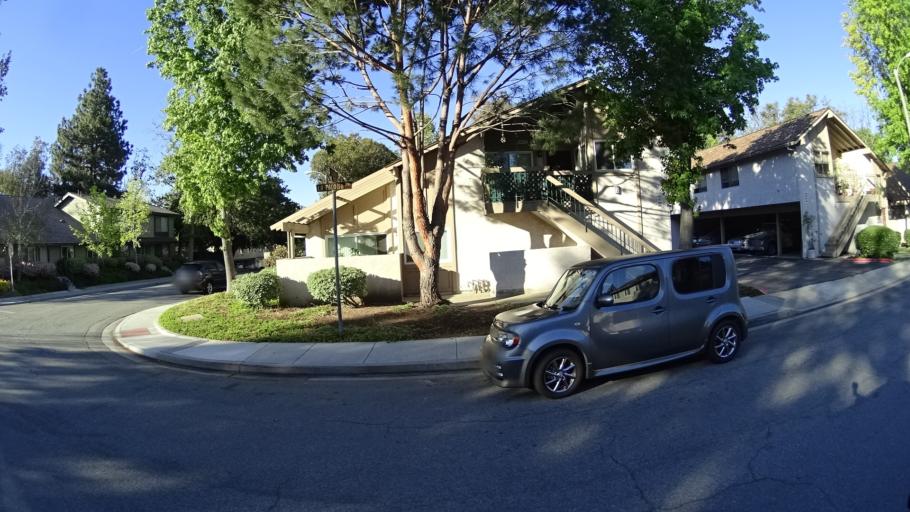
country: US
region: California
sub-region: Ventura County
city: Casa Conejo
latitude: 34.2152
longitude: -118.8897
